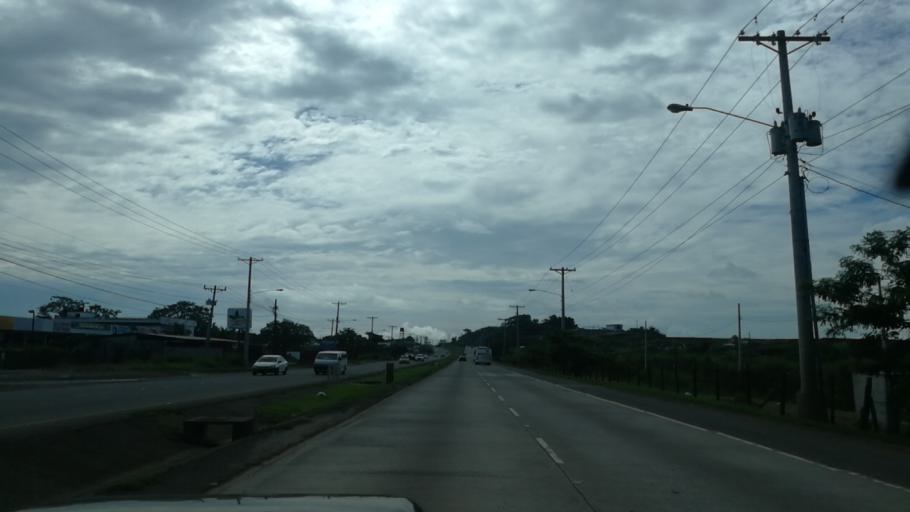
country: PA
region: Panama
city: Pacora
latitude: 9.0981
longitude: -79.2968
